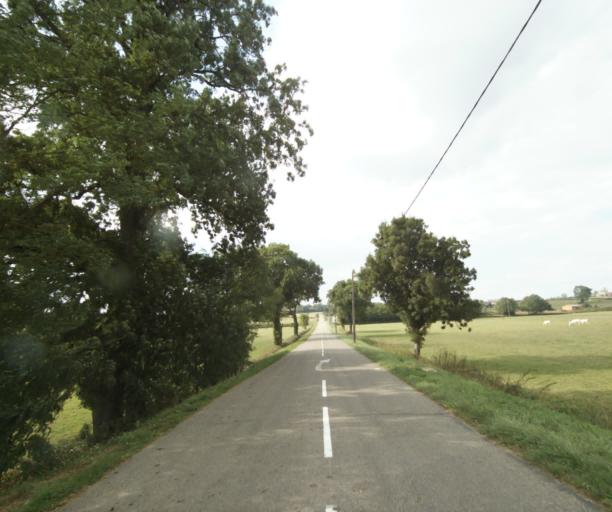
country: FR
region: Bourgogne
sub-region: Departement de Saone-et-Loire
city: Palinges
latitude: 46.5073
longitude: 4.1852
